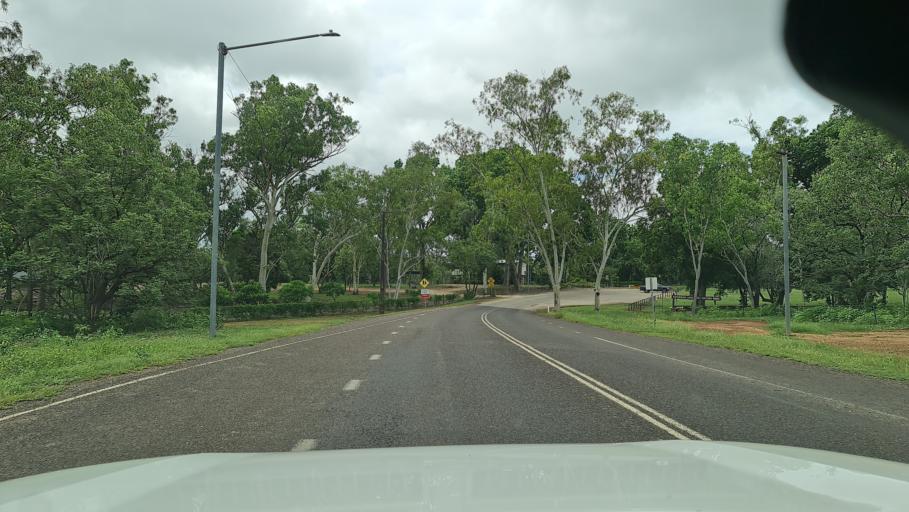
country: AU
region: Northern Territory
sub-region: Katherine
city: Katherine
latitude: -14.4870
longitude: 132.2512
